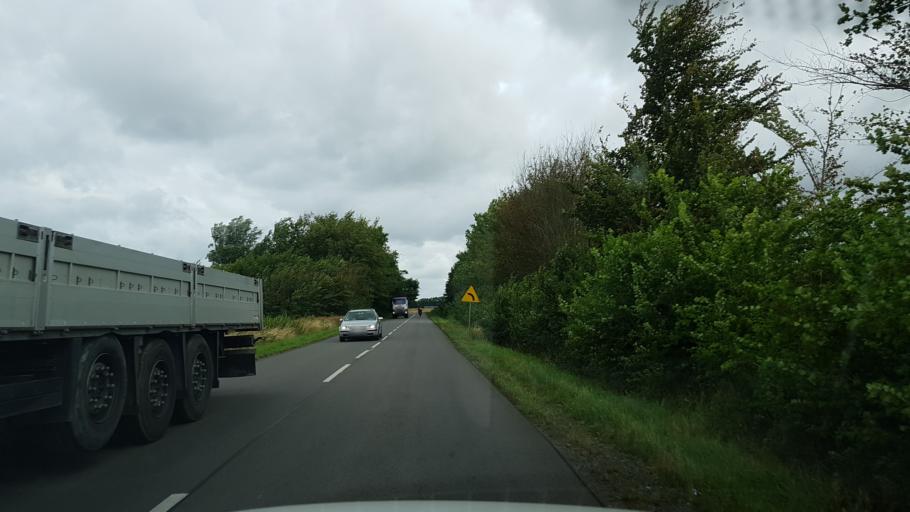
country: PL
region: West Pomeranian Voivodeship
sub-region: Powiat gryficki
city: Rewal
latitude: 54.0634
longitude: 15.0268
